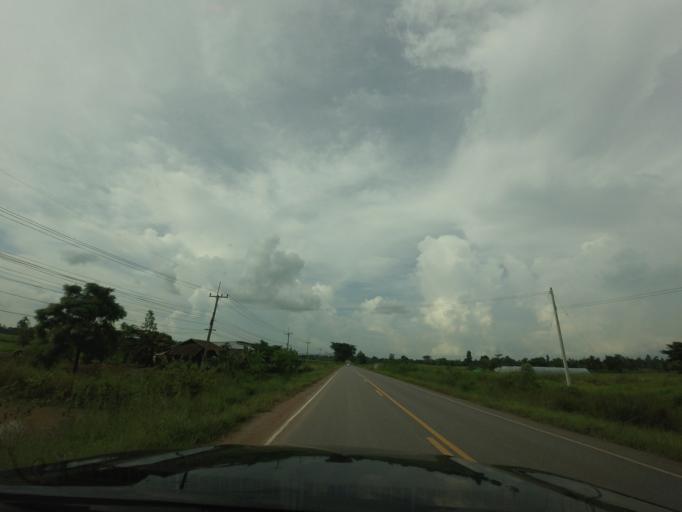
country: TH
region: Changwat Nong Bua Lamphu
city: Suwannakhuha
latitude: 17.4213
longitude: 102.3362
